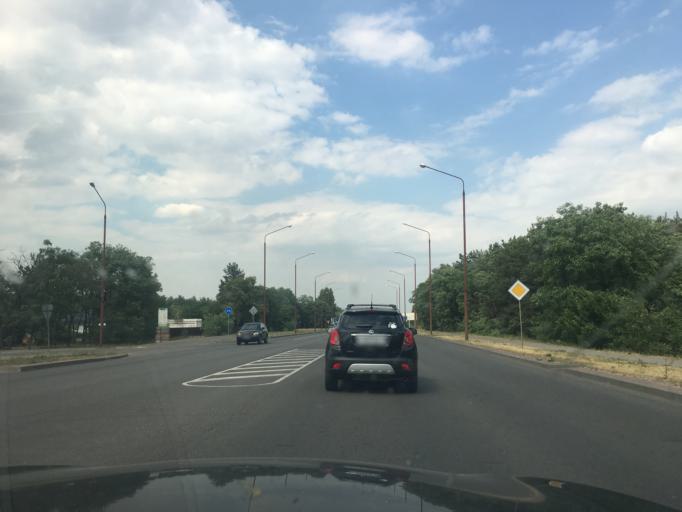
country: BY
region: Brest
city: Brest
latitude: 52.1442
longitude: 23.6831
